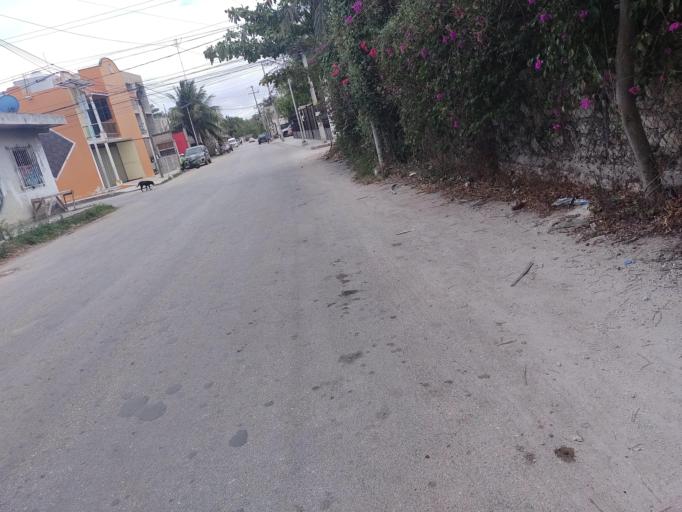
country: MX
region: Quintana Roo
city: Tulum
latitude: 20.2074
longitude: -87.4721
